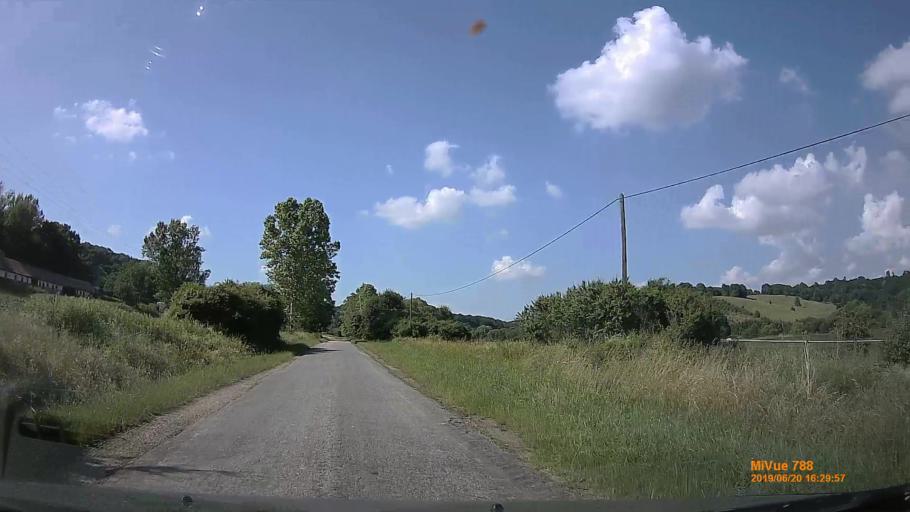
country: HU
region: Baranya
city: Buekkoesd
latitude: 46.1654
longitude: 18.0581
